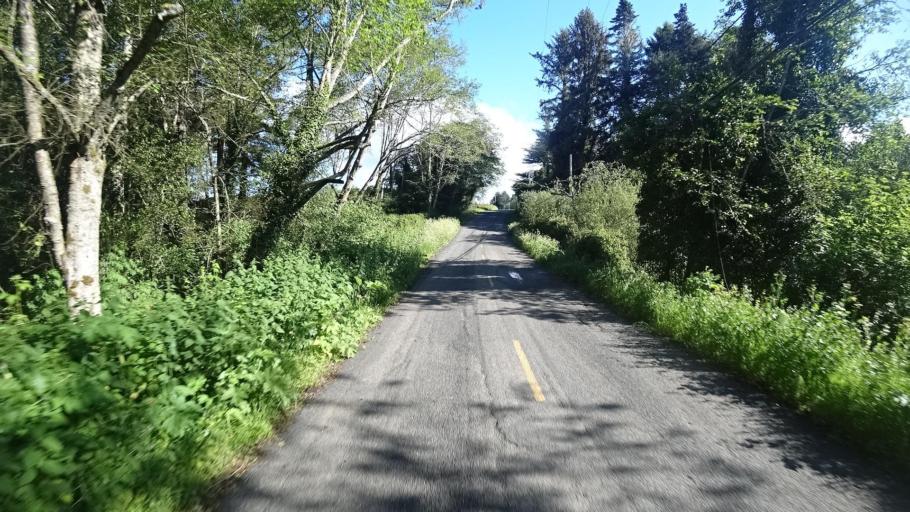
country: US
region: California
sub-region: Humboldt County
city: Westhaven-Moonstone
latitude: 40.9989
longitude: -124.1007
